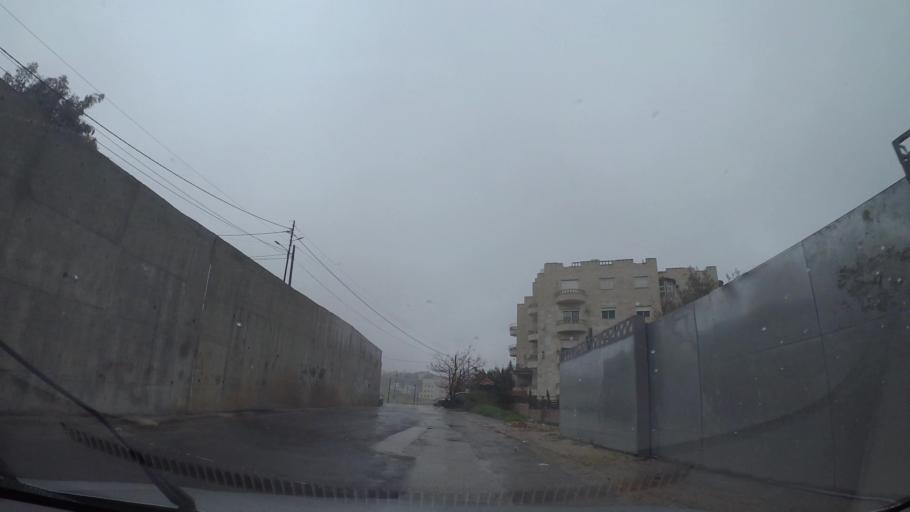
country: JO
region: Amman
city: Al Jubayhah
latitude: 32.0045
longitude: 35.8303
